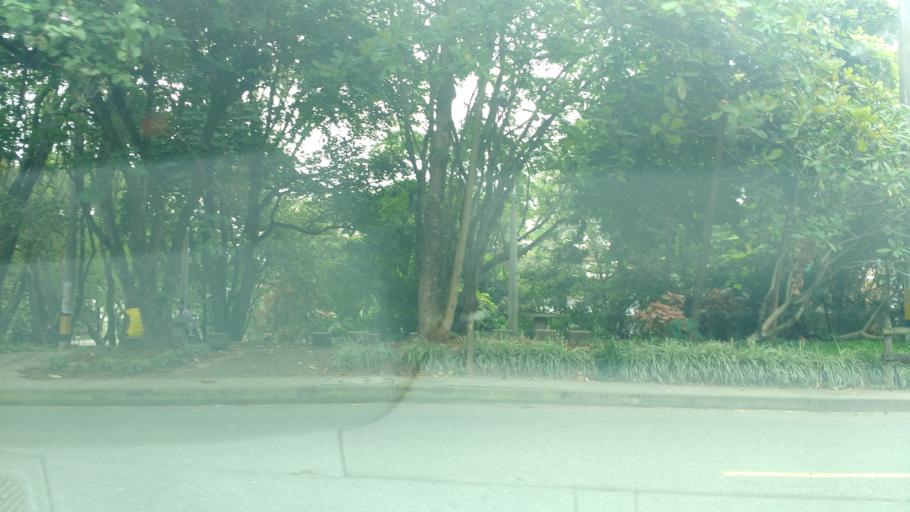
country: CO
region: Antioquia
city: Medellin
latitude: 6.2588
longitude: -75.6081
